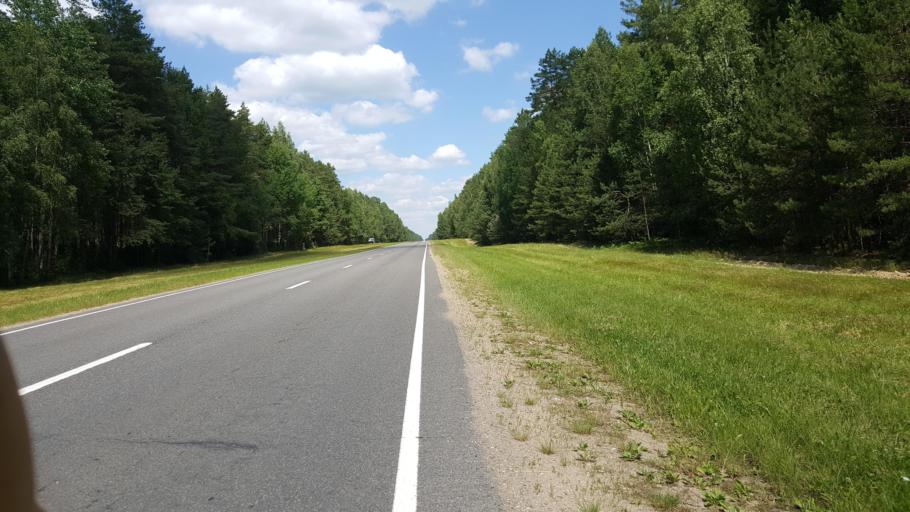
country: BY
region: Brest
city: Kamyanyuki
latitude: 52.5099
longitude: 23.7885
